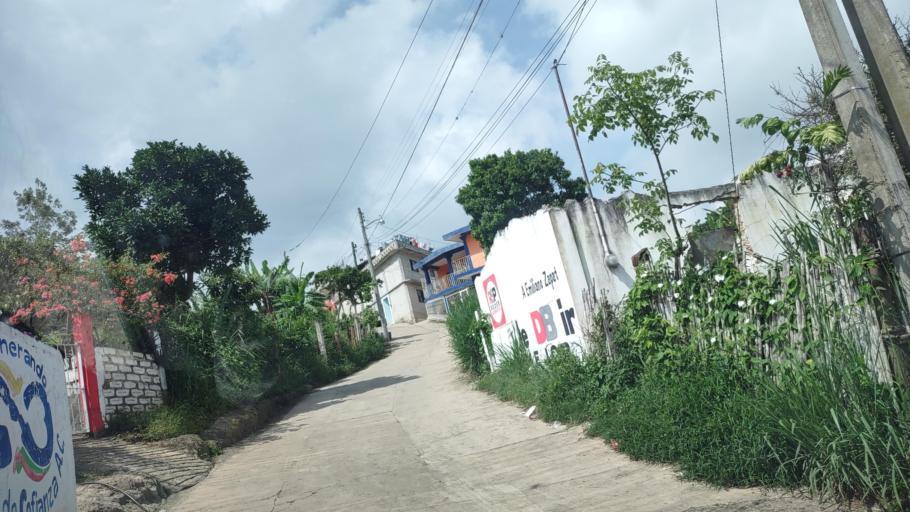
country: MX
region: Veracruz
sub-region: Emiliano Zapata
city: Jacarandas
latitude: 19.4687
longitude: -96.8373
